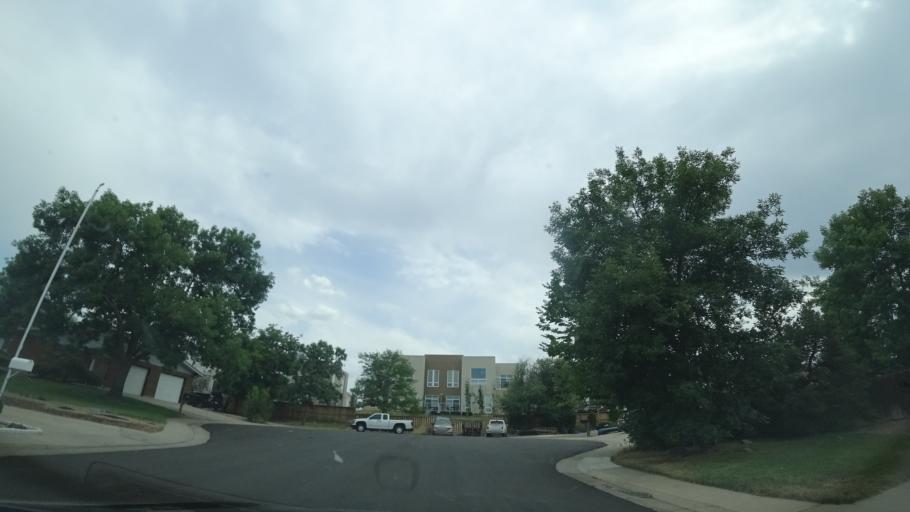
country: US
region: Colorado
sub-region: Jefferson County
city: Lakewood
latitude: 39.7132
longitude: -105.0862
